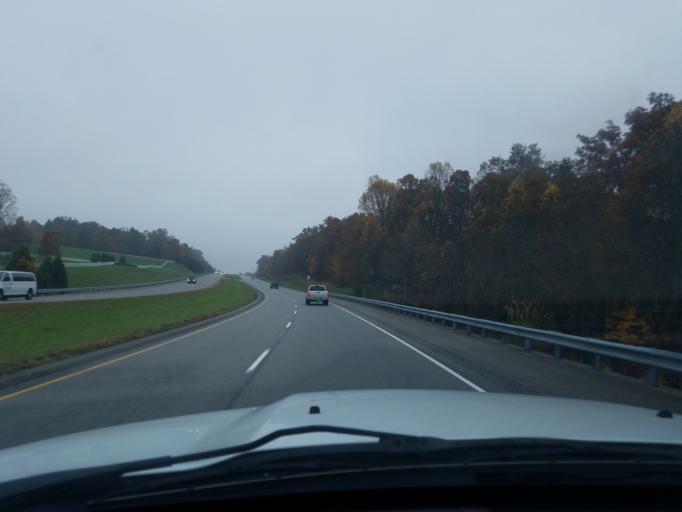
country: US
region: Kentucky
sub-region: Hardin County
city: Elizabethtown
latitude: 37.6403
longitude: -85.8369
